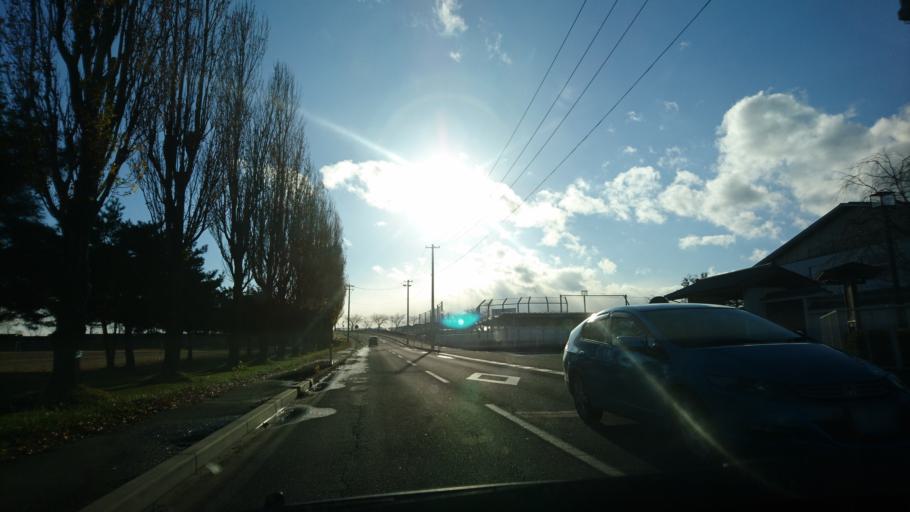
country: JP
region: Iwate
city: Mizusawa
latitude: 39.0578
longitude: 141.1398
